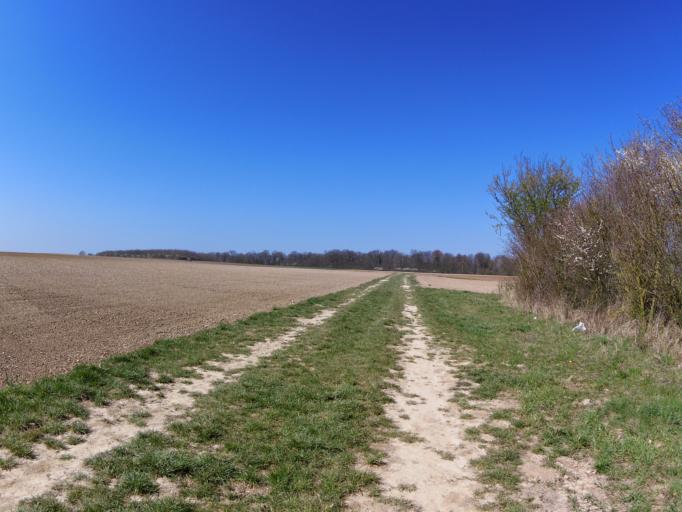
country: DE
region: Bavaria
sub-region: Regierungsbezirk Unterfranken
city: Kurnach
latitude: 49.8376
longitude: 10.0718
